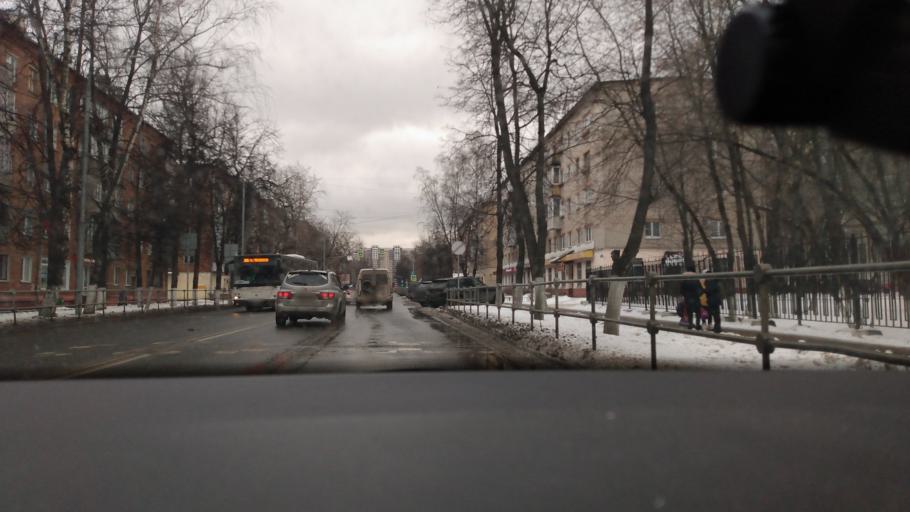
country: RU
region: Moskovskaya
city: Balashikha
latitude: 55.8022
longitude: 37.9348
